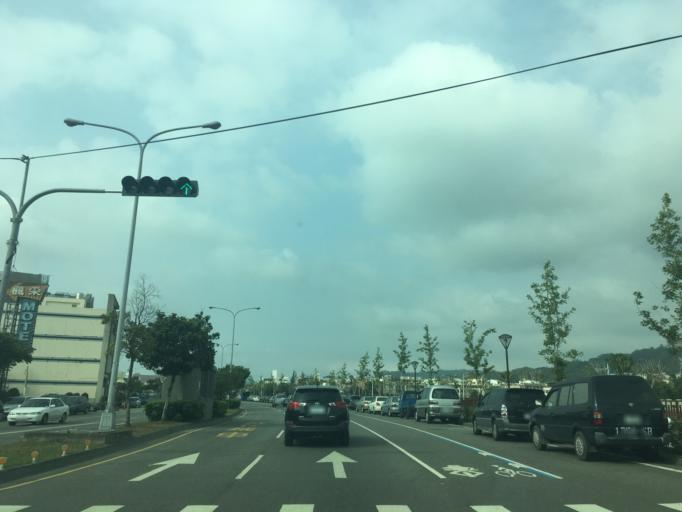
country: TW
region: Taiwan
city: Fengyuan
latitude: 24.2389
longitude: 120.7275
